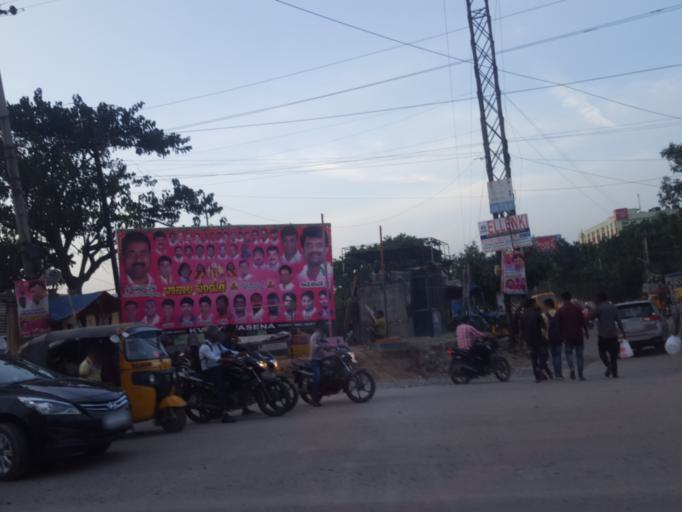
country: IN
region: Telangana
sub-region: Rangareddi
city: Kukatpalli
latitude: 17.5409
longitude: 78.3638
